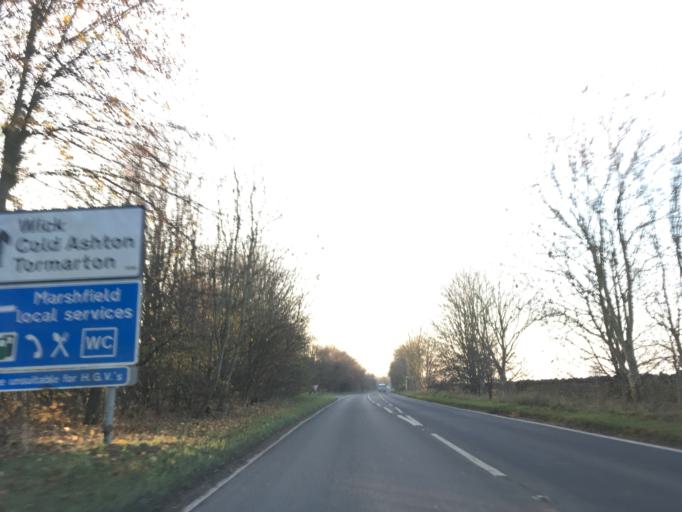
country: GB
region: England
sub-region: South Gloucestershire
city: Marshfield
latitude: 51.4633
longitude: -2.3084
